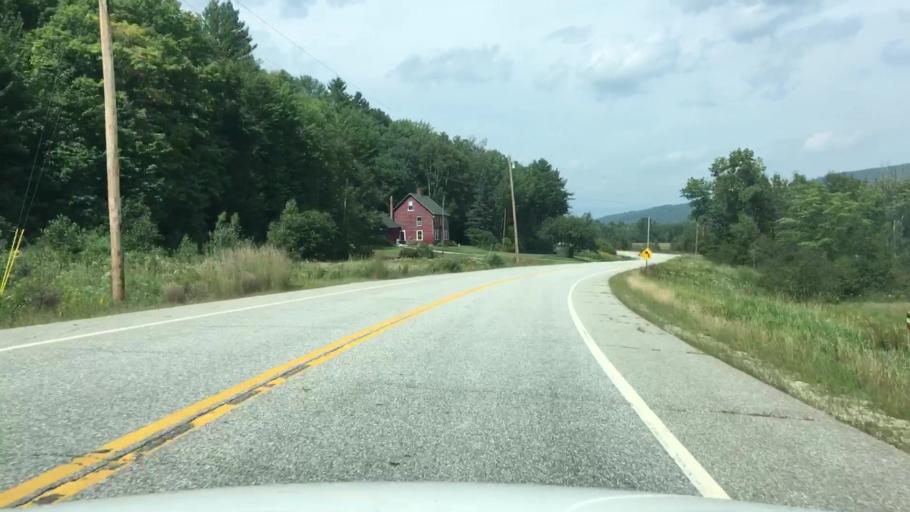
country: US
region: Maine
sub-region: Oxford County
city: Rumford
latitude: 44.5515
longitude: -70.7098
